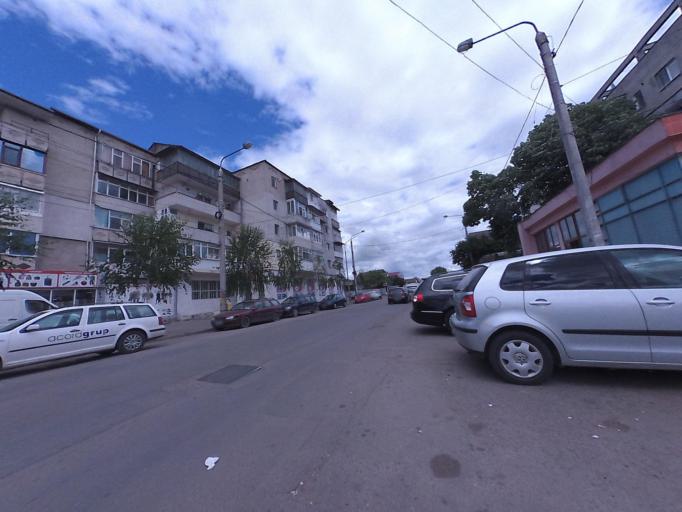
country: RO
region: Vaslui
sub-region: Municipiul Barlad
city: Barlad
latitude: 46.2161
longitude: 27.6733
